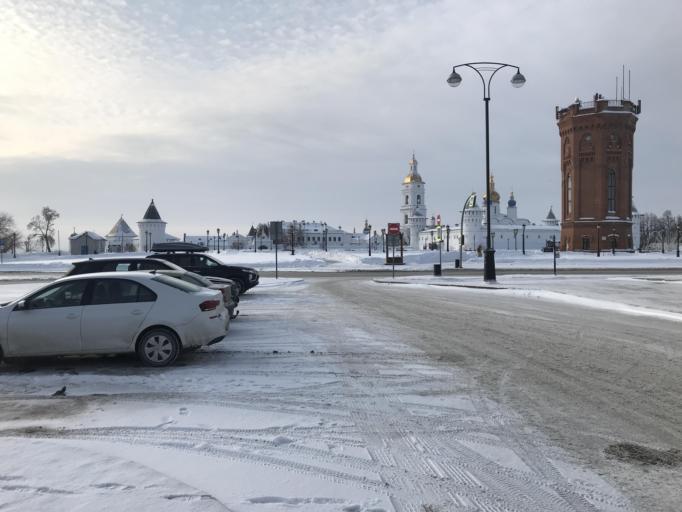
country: RU
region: Tjumen
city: Tobol'sk
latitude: 58.2008
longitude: 68.2560
